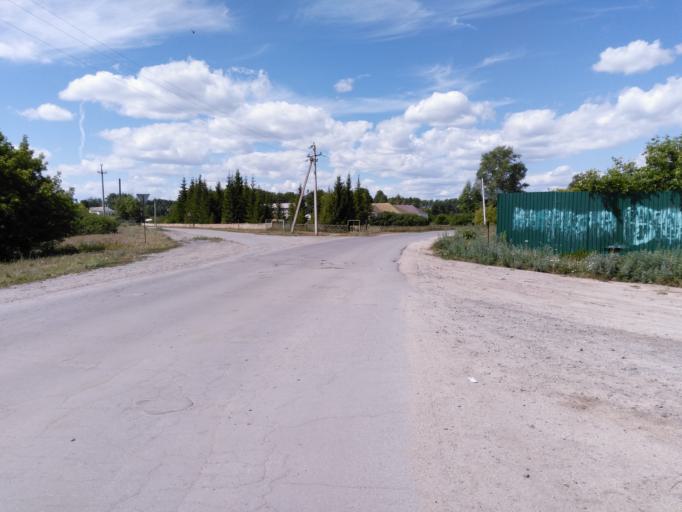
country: RU
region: Bashkortostan
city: Akhunovo
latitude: 54.2109
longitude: 59.6024
